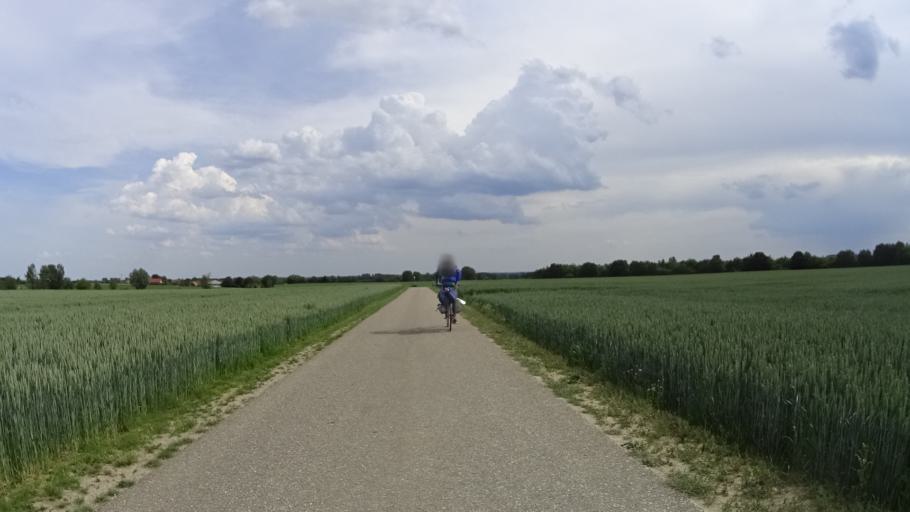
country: DE
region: Bavaria
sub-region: Lower Bavaria
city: Aholfing
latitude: 48.9836
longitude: 12.4481
